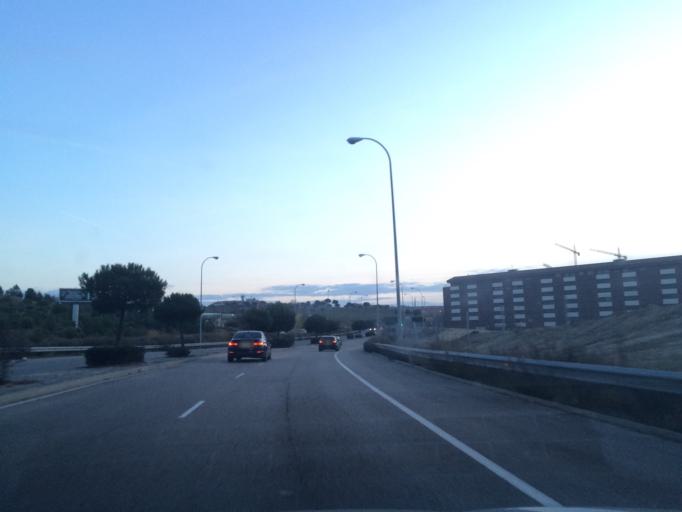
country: ES
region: Madrid
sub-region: Provincia de Madrid
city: Fuencarral-El Pardo
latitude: 40.4983
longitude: -3.7199
